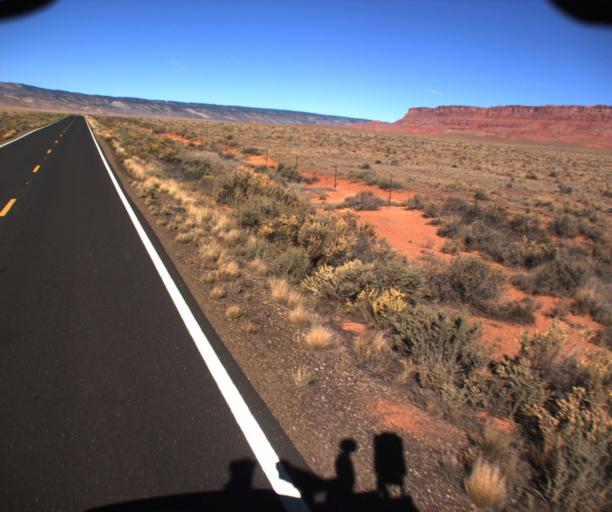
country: US
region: Arizona
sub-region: Coconino County
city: Page
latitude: 36.7051
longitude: -111.9478
